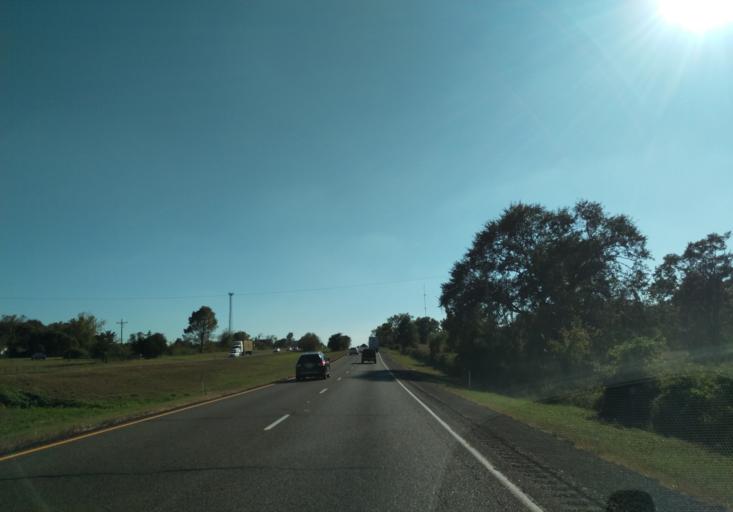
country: US
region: Texas
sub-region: Grimes County
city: Navasota
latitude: 30.2605
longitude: -96.0432
